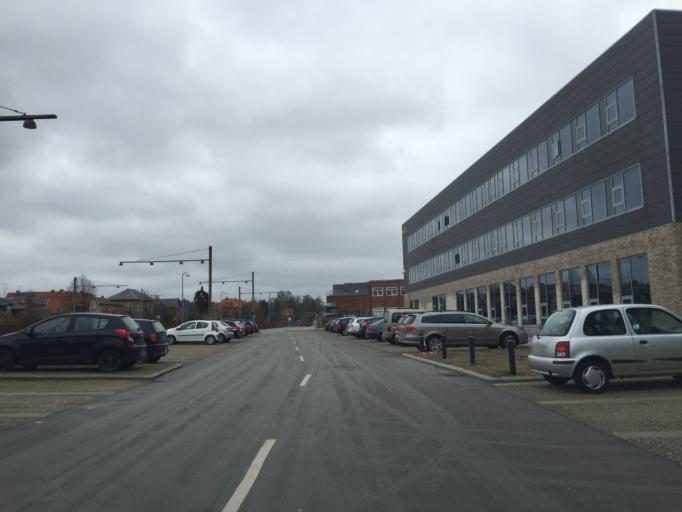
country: DK
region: Capital Region
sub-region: Hillerod Kommune
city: Hillerod
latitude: 55.9295
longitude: 12.3126
